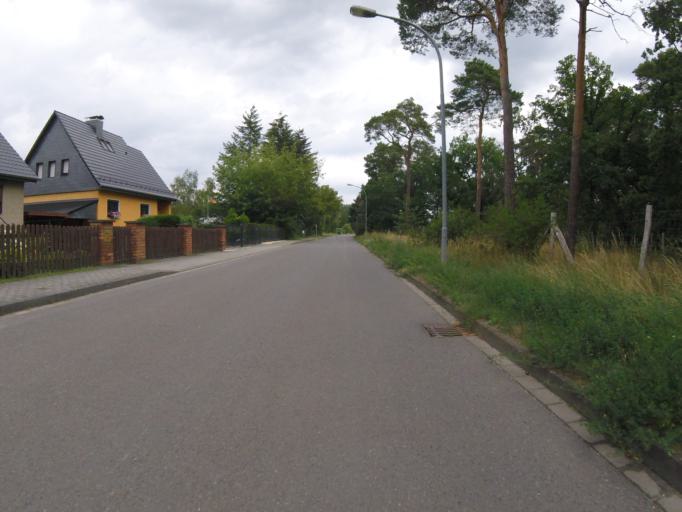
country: DE
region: Brandenburg
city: Konigs Wusterhausen
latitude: 52.2998
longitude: 13.6381
